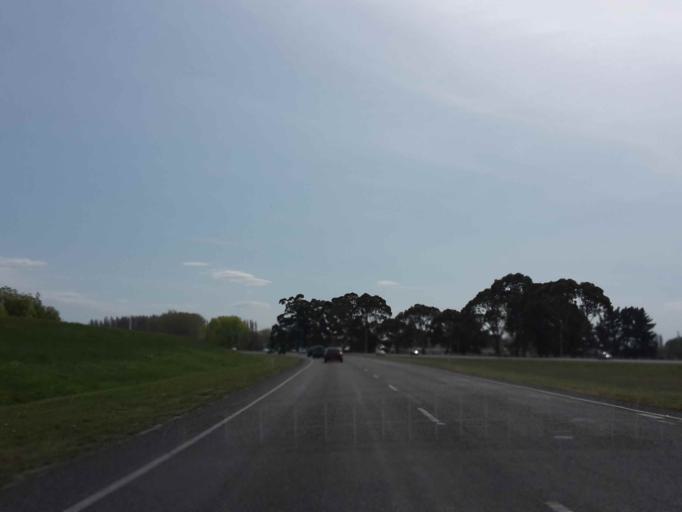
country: NZ
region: Canterbury
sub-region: Waimakariri District
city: Kaiapoi
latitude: -43.4254
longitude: 172.6477
